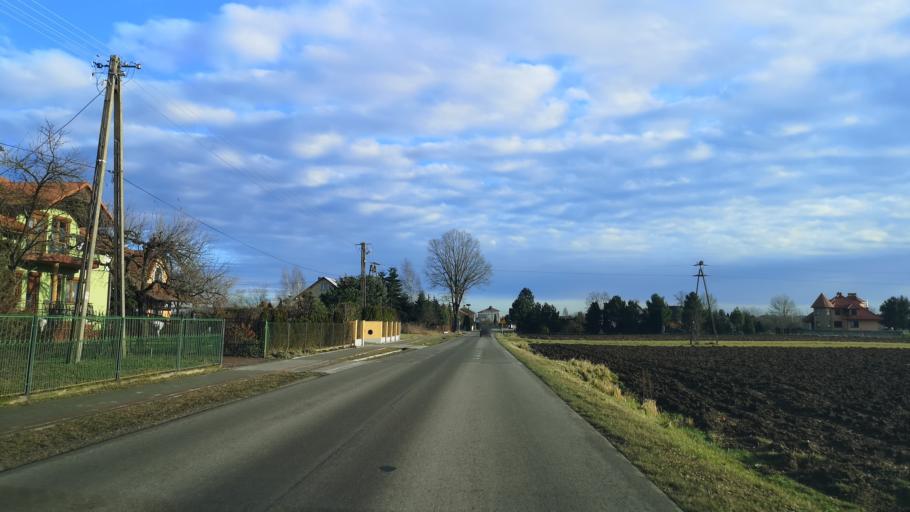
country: PL
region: Subcarpathian Voivodeship
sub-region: Powiat lezajski
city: Piskorowice
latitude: 50.2437
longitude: 22.5120
